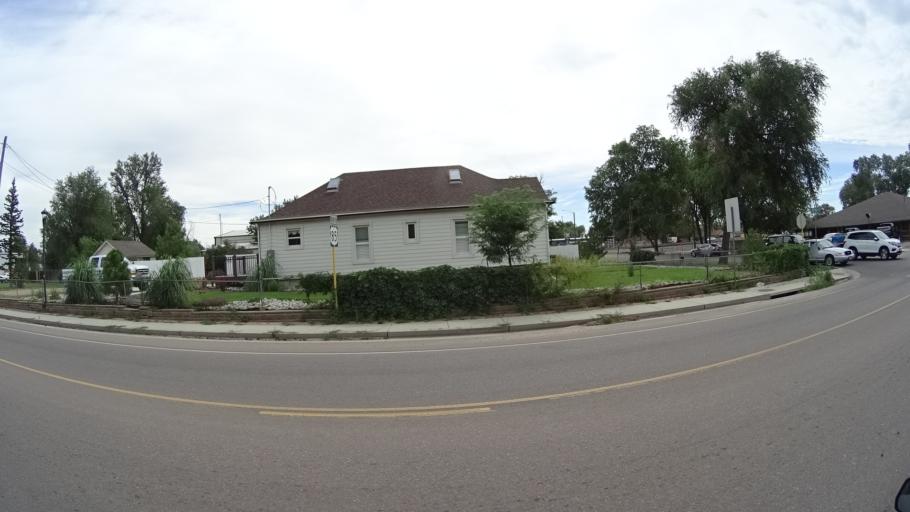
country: US
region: Colorado
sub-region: El Paso County
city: Fountain
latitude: 38.6812
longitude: -104.7046
